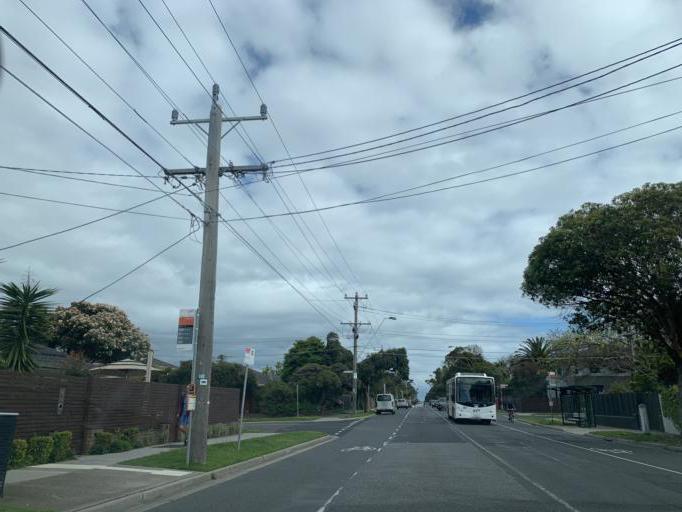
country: AU
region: Victoria
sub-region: Bayside
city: Cheltenham
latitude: -37.9764
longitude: 145.0537
